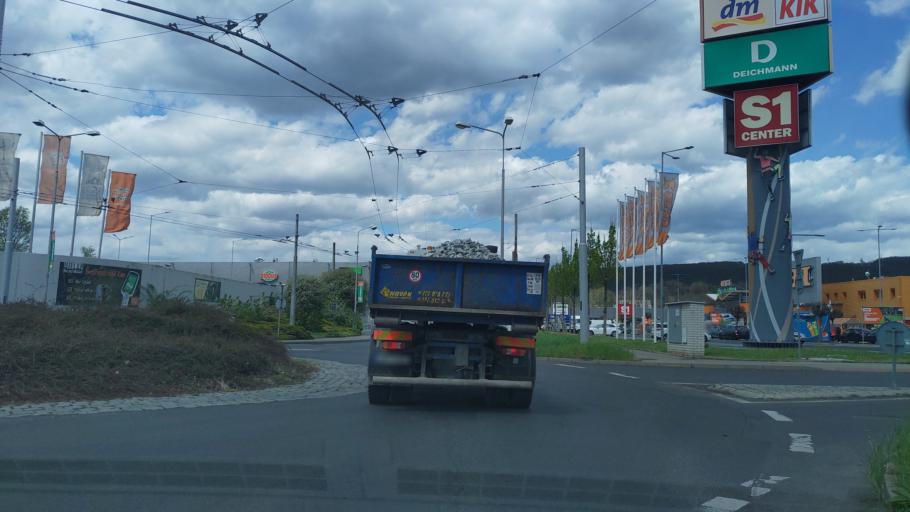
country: CZ
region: Ustecky
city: Trmice
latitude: 50.6503
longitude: 14.0041
